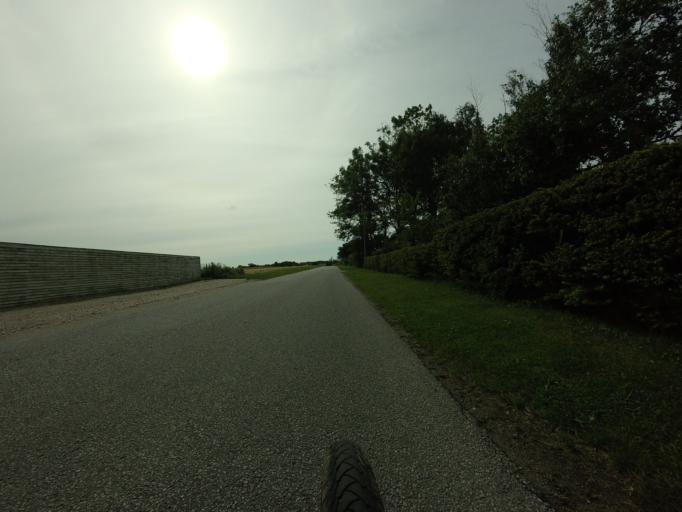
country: DK
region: North Denmark
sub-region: Hjorring Kommune
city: Hjorring
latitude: 57.4336
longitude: 9.9023
